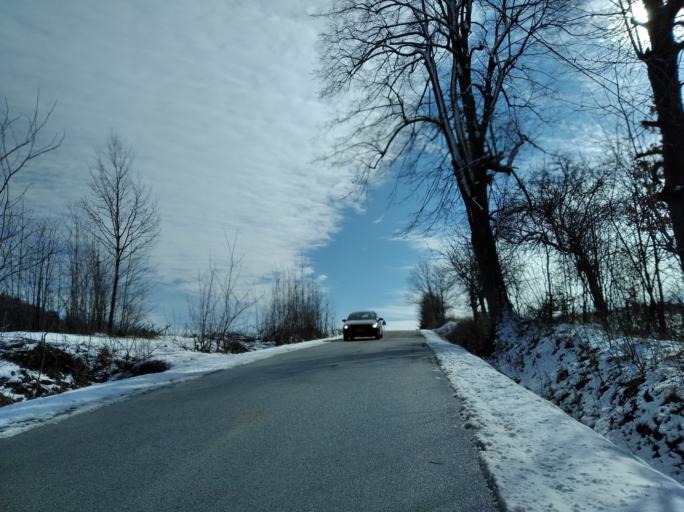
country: PL
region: Subcarpathian Voivodeship
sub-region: Powiat brzozowski
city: Jablonica Polska
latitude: 49.7280
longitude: 21.8998
